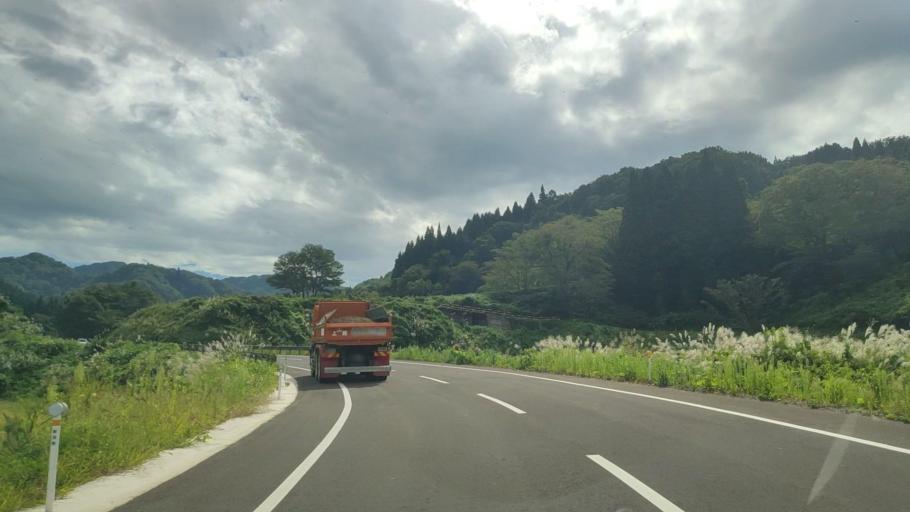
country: JP
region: Niigata
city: Arai
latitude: 36.9494
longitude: 138.2816
